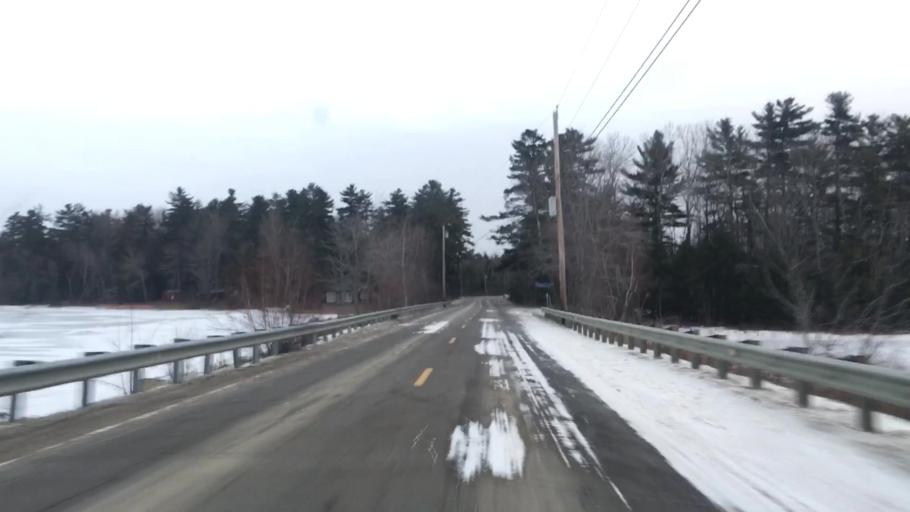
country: US
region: Maine
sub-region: Hancock County
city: Ellsworth
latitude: 44.6150
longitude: -68.3862
